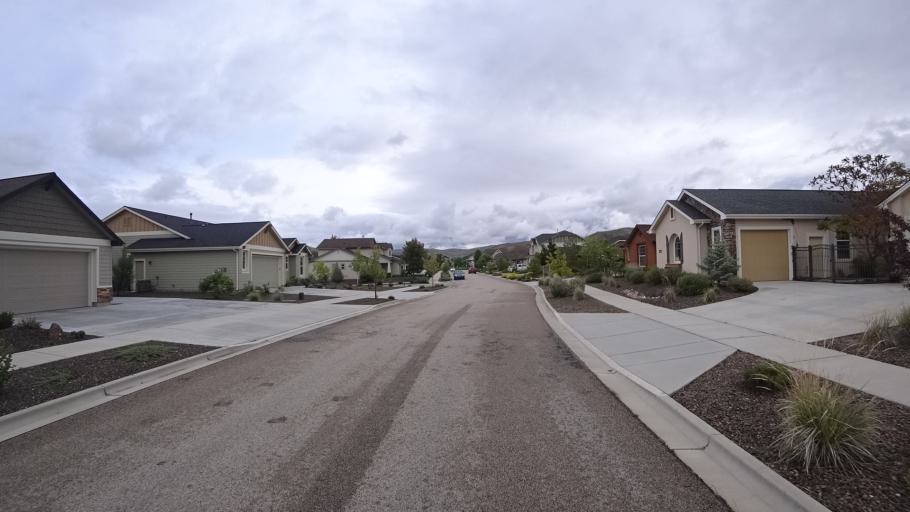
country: US
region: Idaho
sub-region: Ada County
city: Eagle
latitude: 43.7687
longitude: -116.2640
